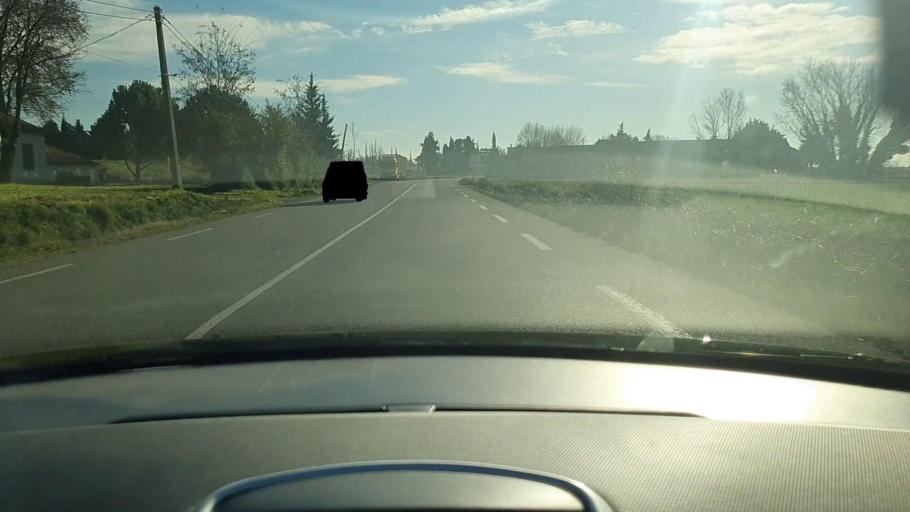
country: FR
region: Languedoc-Roussillon
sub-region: Departement du Gard
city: Fourques
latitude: 43.7391
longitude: 4.6114
